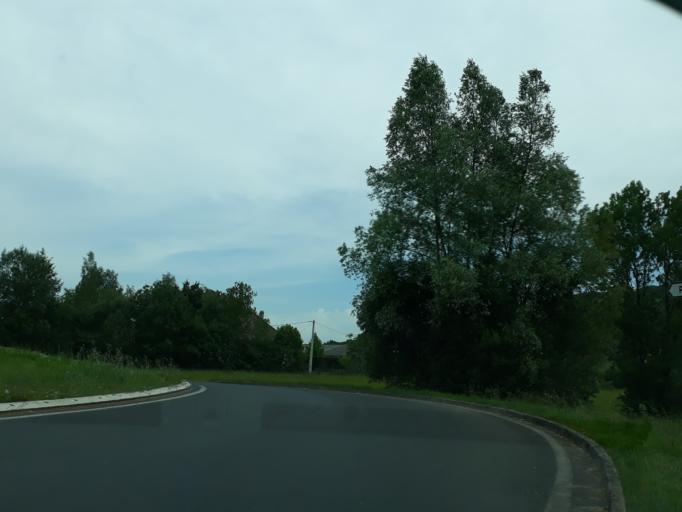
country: FR
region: Limousin
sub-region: Departement de la Correze
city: Mansac
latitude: 45.1265
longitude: 1.3692
